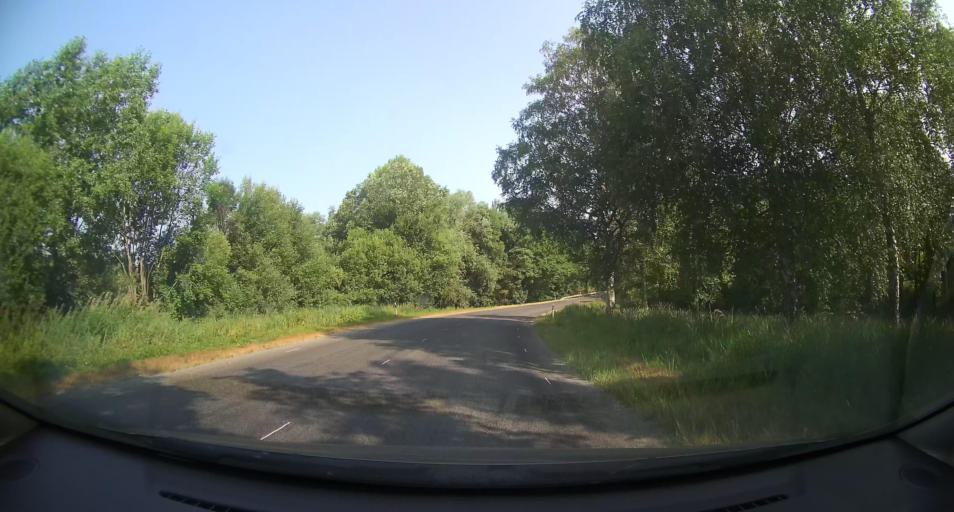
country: EE
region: Paernumaa
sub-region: Audru vald
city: Audru
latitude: 58.4425
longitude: 24.3071
